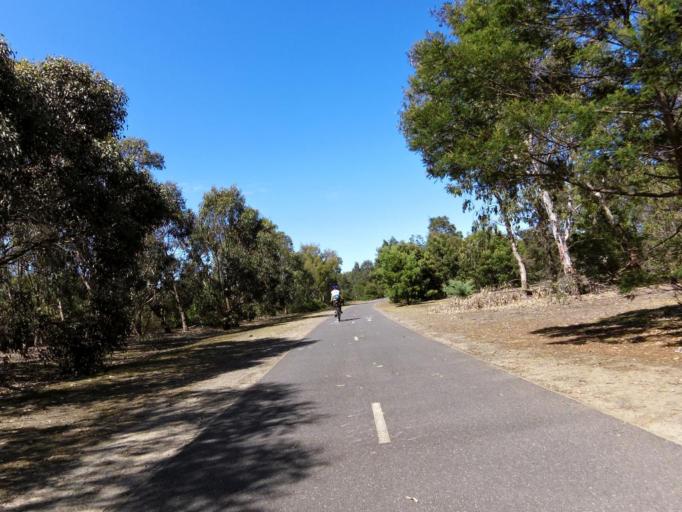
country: AU
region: Victoria
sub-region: Kingston
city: Carrum
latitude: -38.0894
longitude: 145.1456
